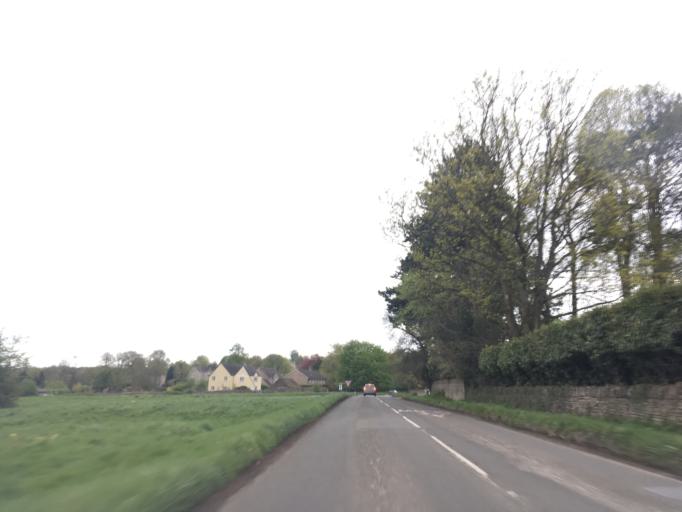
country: GB
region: England
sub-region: Gloucestershire
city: Stroud
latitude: 51.7254
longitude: -2.2139
